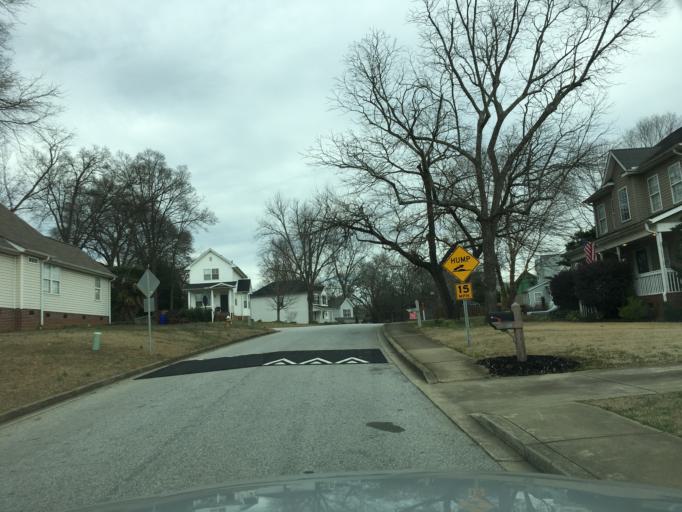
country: US
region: South Carolina
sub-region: Greenville County
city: Greenville
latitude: 34.8606
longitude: -82.4004
